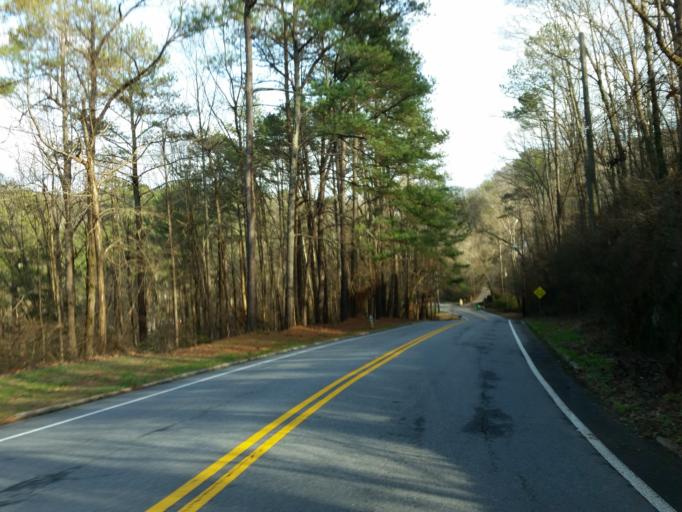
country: US
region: Georgia
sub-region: Fulton County
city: Sandy Springs
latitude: 33.9459
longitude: -84.3988
